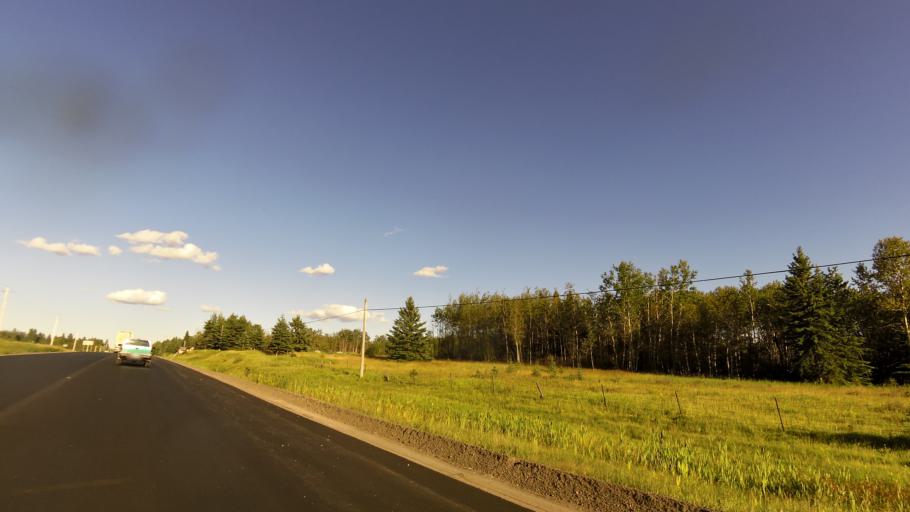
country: CA
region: Ontario
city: Dryden
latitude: 49.8151
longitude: -92.8914
